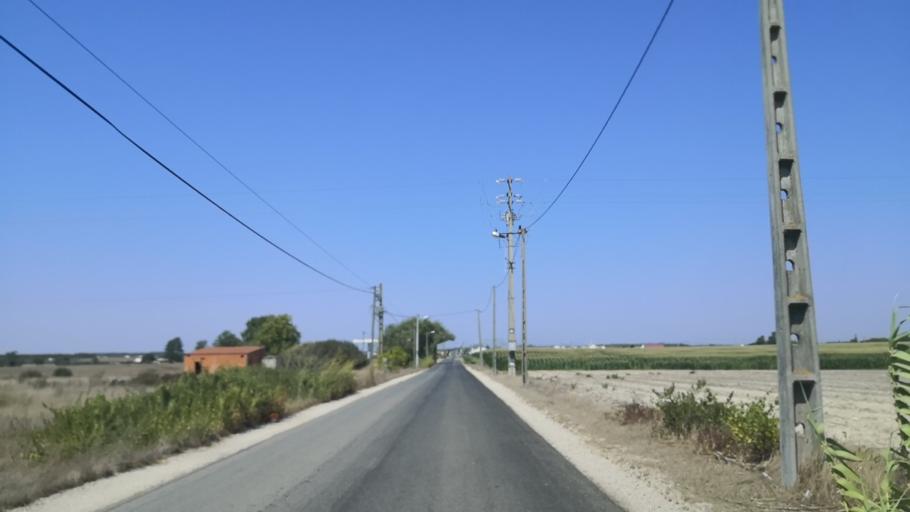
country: PT
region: Santarem
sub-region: Benavente
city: Poceirao
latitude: 38.6943
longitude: -8.7278
